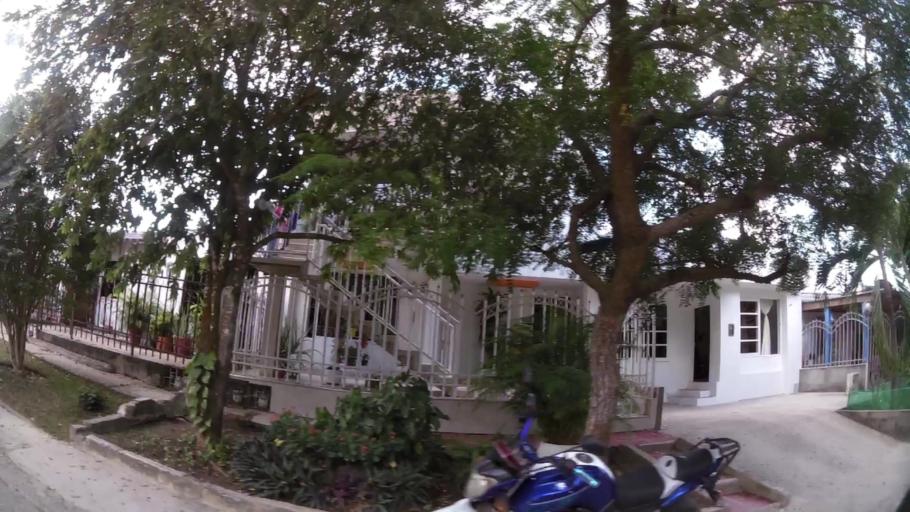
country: CO
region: Bolivar
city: Cartagena
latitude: 10.3699
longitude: -75.4606
